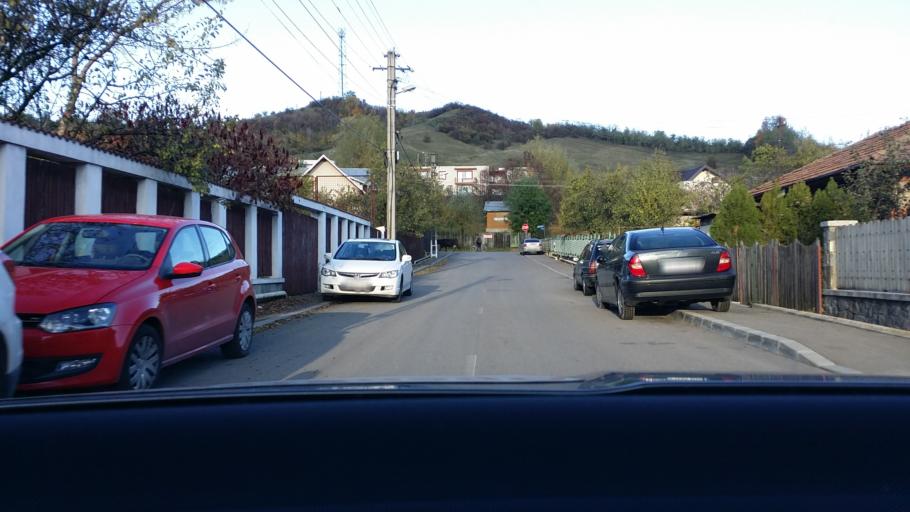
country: RO
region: Prahova
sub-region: Municipiul Campina
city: Campina
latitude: 45.1384
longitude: 25.7411
